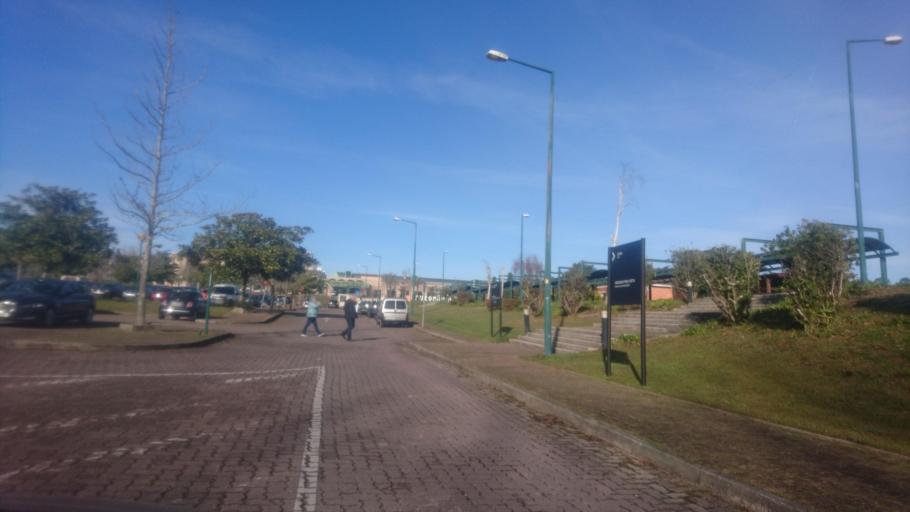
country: PT
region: Aveiro
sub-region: Santa Maria da Feira
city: Rio Meao
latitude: 40.9332
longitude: -8.5757
